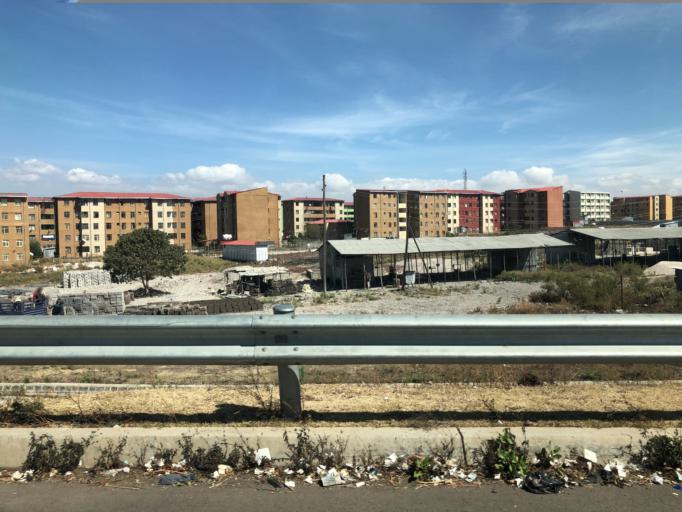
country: ET
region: Adis Abeba
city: Addis Ababa
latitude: 8.8633
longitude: 38.8230
